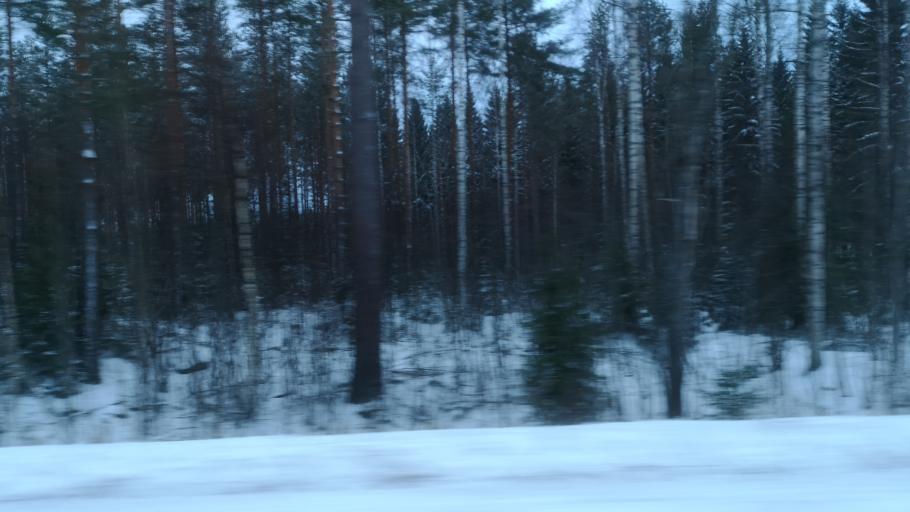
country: FI
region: Southern Savonia
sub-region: Savonlinna
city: Enonkoski
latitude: 62.1094
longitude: 28.6176
